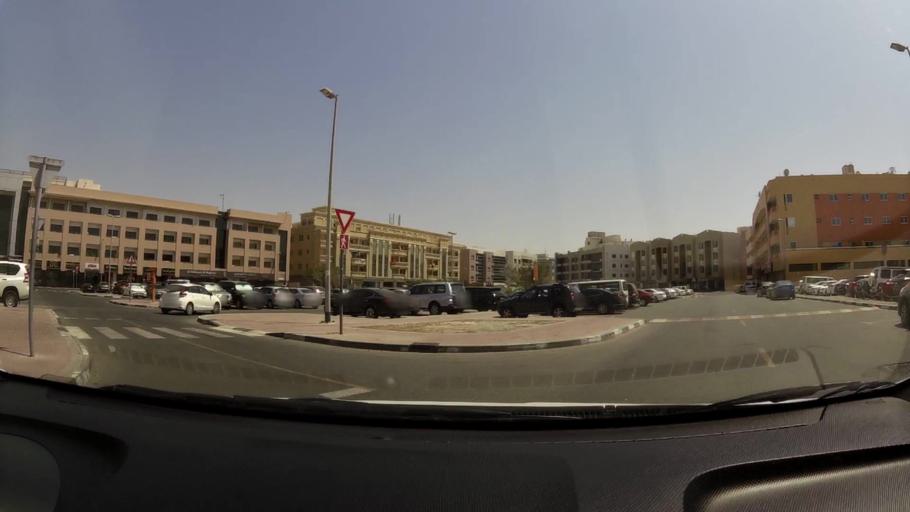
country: AE
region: Ash Shariqah
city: Sharjah
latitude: 25.2824
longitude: 55.3510
